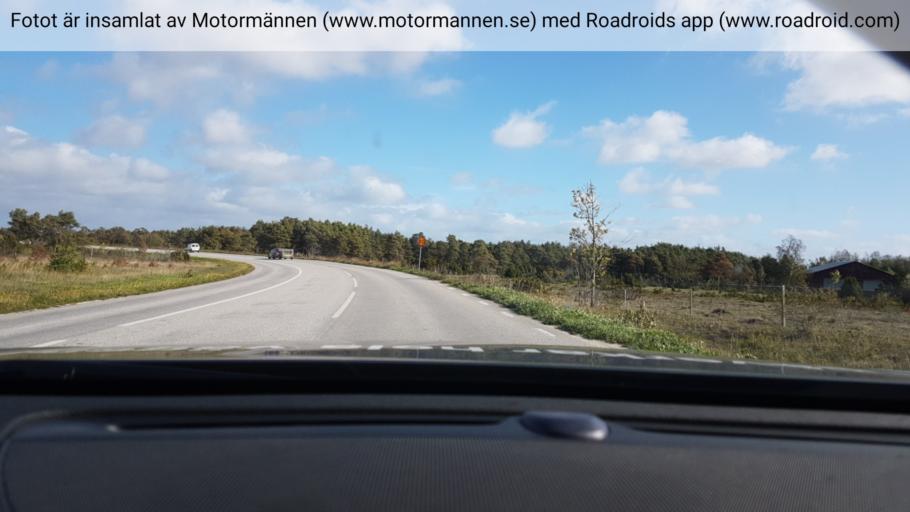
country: SE
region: Gotland
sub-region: Gotland
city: Slite
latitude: 57.8699
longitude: 19.0848
